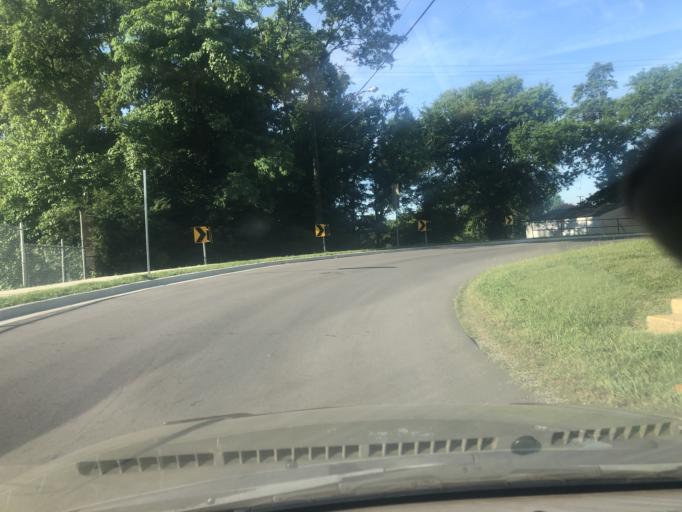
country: US
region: Tennessee
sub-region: Davidson County
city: Lakewood
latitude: 36.2601
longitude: -86.6535
